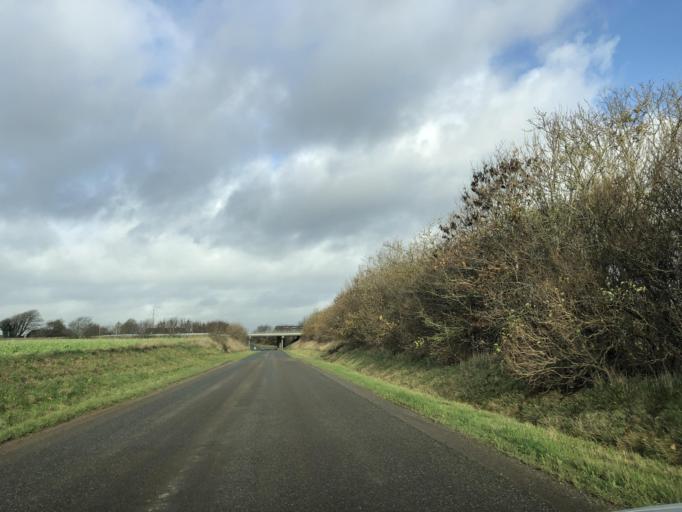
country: DK
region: South Denmark
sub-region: Esbjerg Kommune
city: Bramming
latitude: 55.4220
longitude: 8.6864
